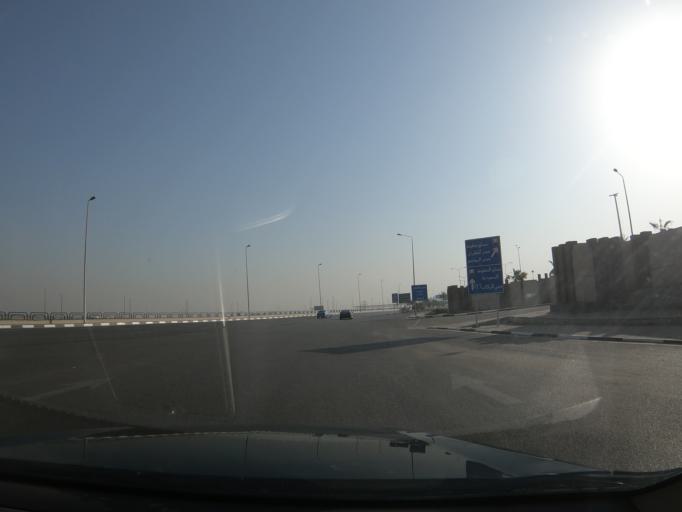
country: EG
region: Muhafazat al Qalyubiyah
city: Al Khankah
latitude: 30.1098
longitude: 31.3868
